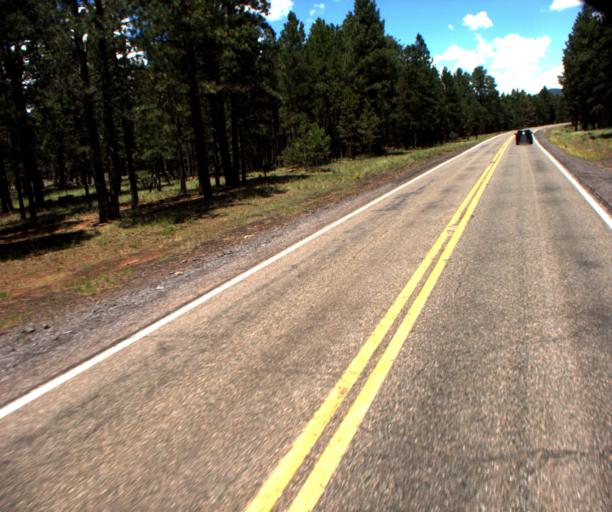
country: US
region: Arizona
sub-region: Coconino County
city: Flagstaff
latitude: 35.3172
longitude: -111.7751
